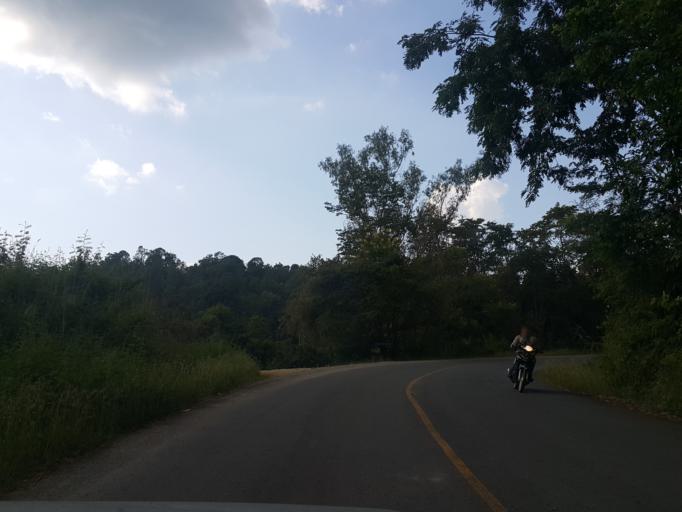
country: TH
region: Chiang Mai
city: Mae Chaem
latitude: 18.5554
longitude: 98.3916
